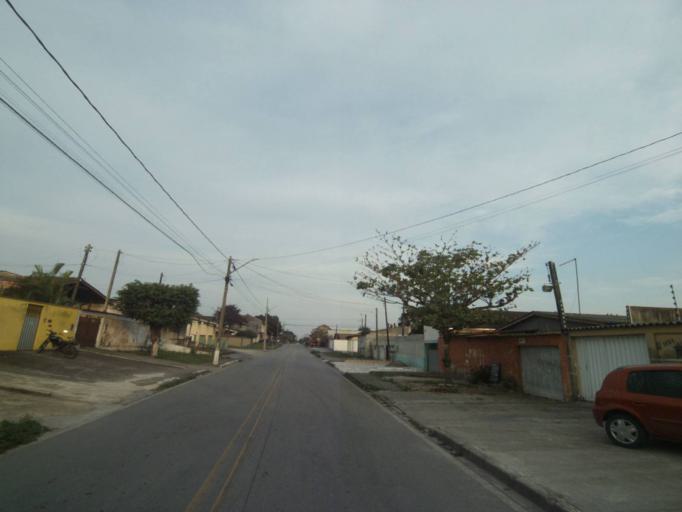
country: BR
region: Parana
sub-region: Paranagua
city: Paranagua
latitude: -25.5199
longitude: -48.5400
